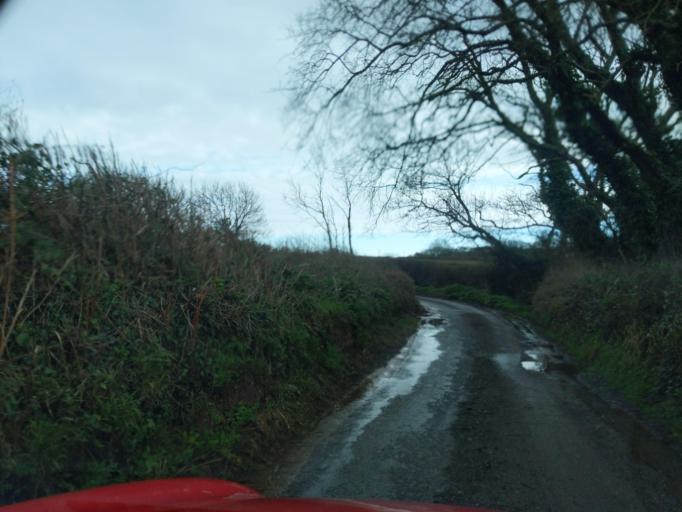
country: GB
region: England
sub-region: Devon
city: Salcombe
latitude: 50.2592
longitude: -3.6800
